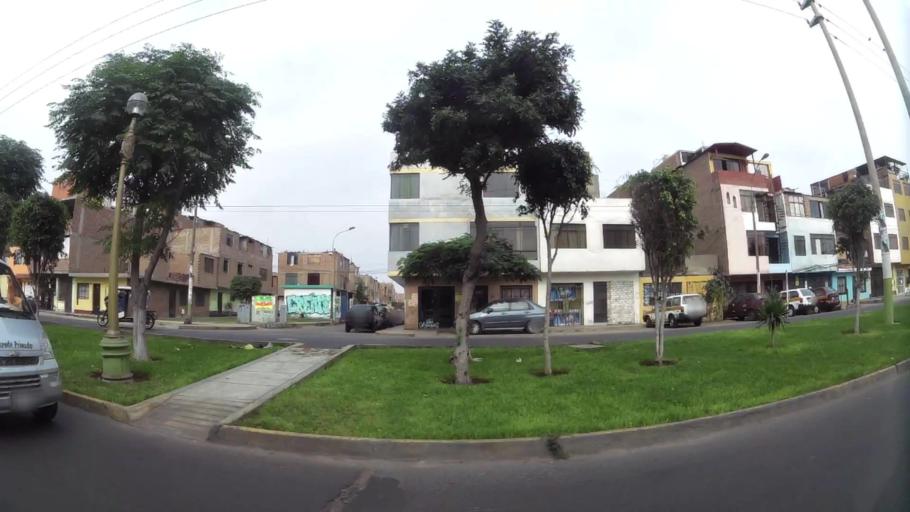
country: PE
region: Callao
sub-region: Callao
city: Callao
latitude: -12.0223
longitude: -77.0977
